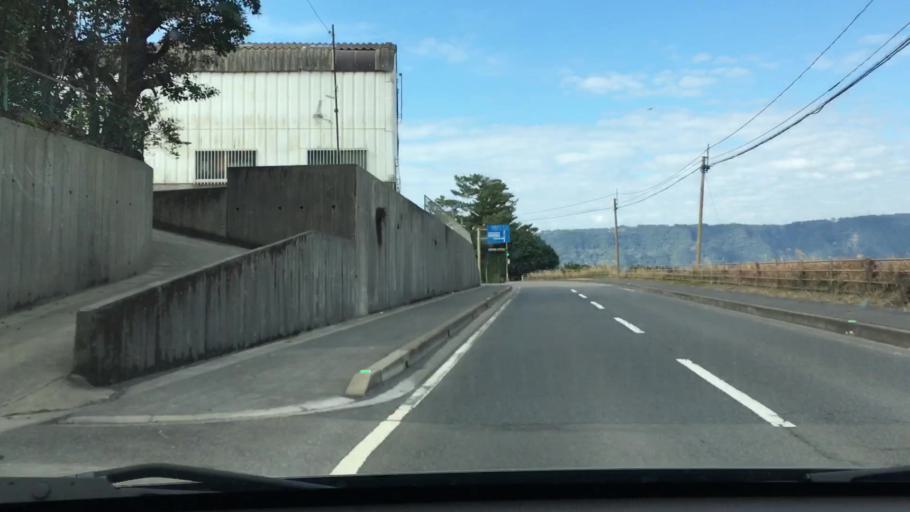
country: JP
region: Kagoshima
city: Kagoshima-shi
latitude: 31.6206
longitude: 130.6353
